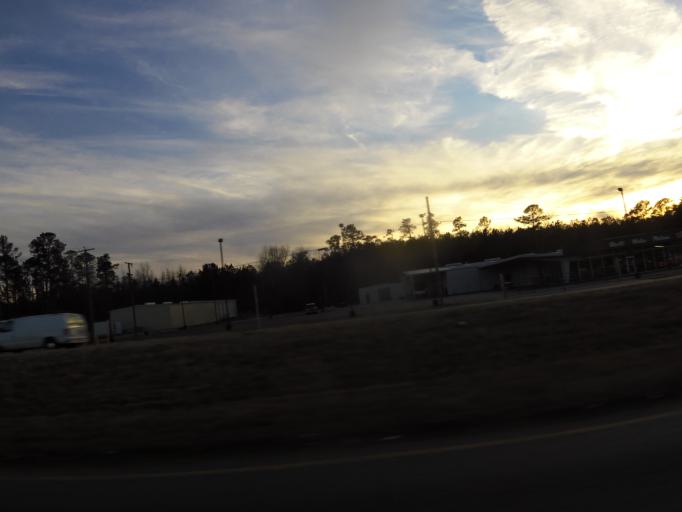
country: US
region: Virginia
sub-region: Southampton County
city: Courtland
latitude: 36.6951
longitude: -77.0352
